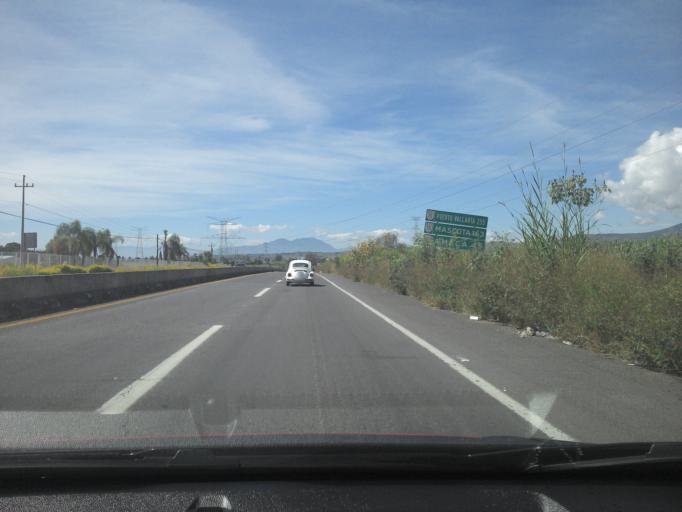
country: MX
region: Jalisco
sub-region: Tala
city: Los Ruisenores
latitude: 20.7125
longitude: -103.6569
